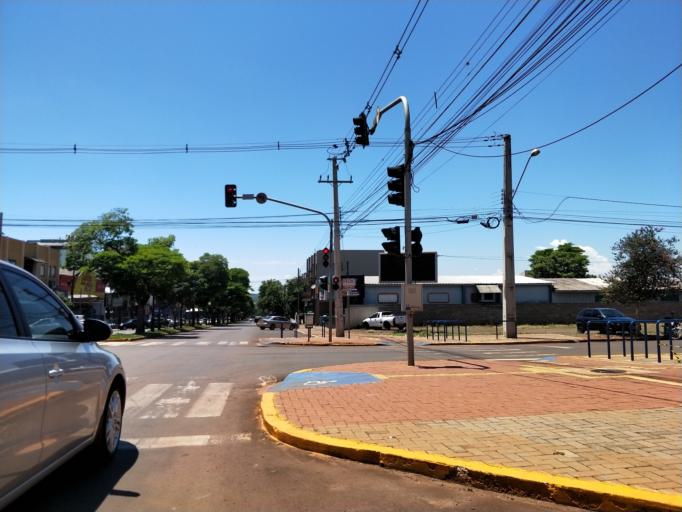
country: BR
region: Parana
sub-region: Marechal Candido Rondon
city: Marechal Candido Rondon
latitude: -24.5645
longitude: -54.0583
